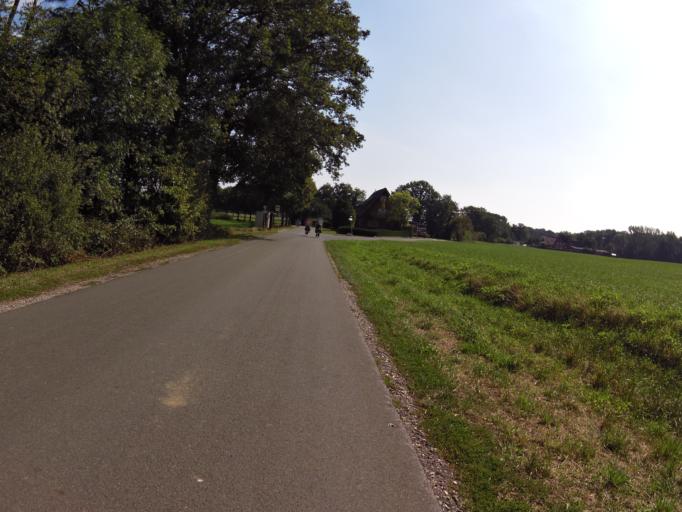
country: DE
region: North Rhine-Westphalia
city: Stadtlohn
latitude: 51.9995
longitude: 6.9514
